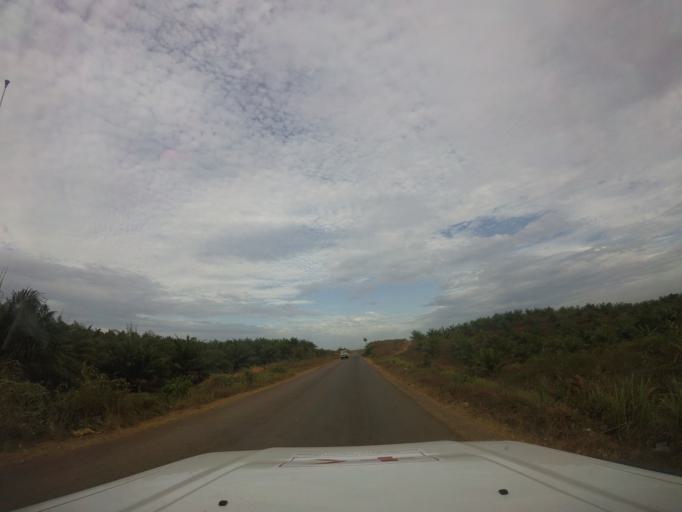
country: LR
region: Bomi
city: Tubmanburg
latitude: 6.7124
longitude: -10.9637
